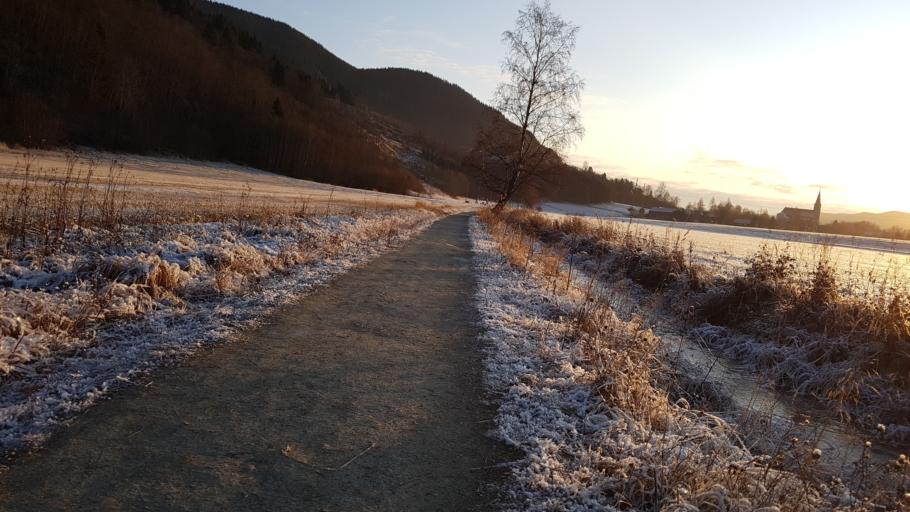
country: NO
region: Sor-Trondelag
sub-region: Melhus
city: Melhus
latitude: 63.2813
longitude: 10.3006
